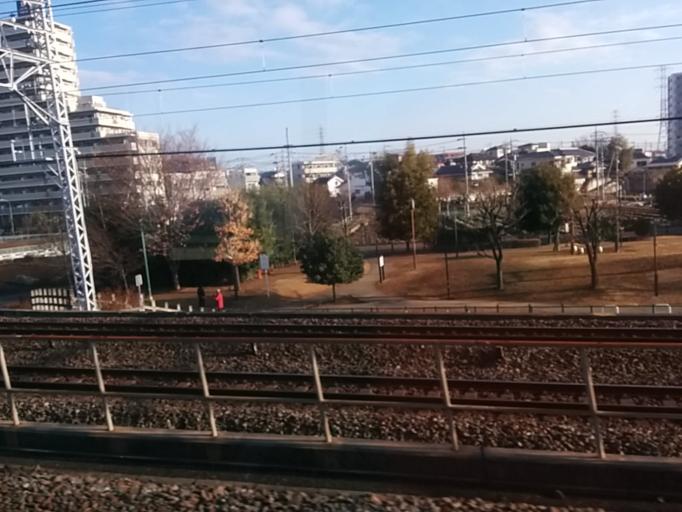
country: JP
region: Saitama
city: Asaka
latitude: 35.7930
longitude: 139.6023
